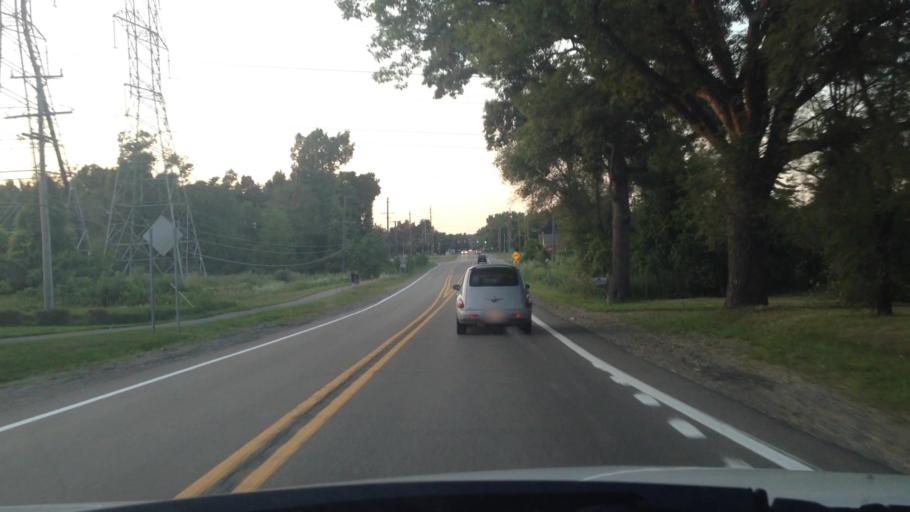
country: US
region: Michigan
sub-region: Oakland County
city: Lake Orion
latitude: 42.7321
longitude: -83.3079
